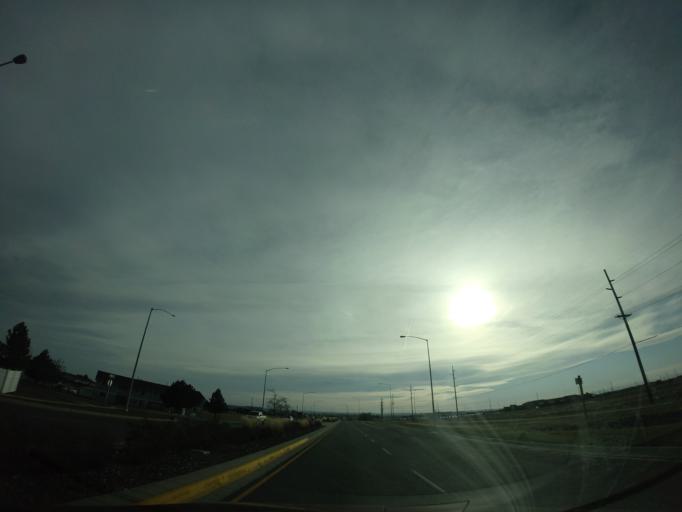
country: US
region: Montana
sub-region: Yellowstone County
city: Billings
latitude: 45.7572
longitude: -108.6176
